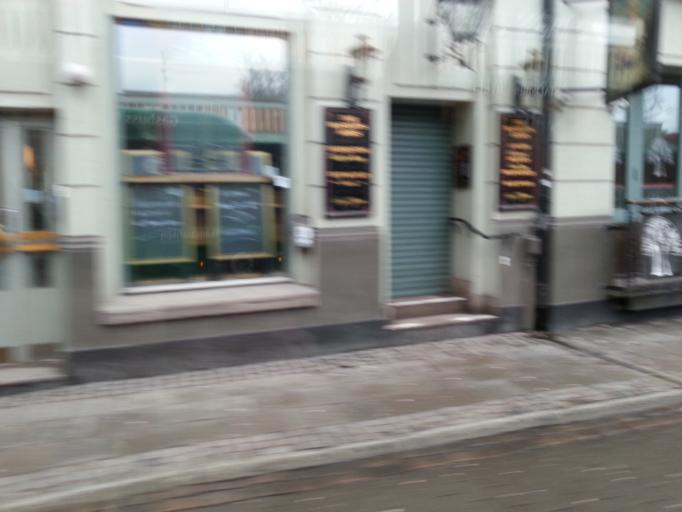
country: SE
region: Skane
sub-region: Lunds Kommun
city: Lund
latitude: 55.7064
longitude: 13.1913
